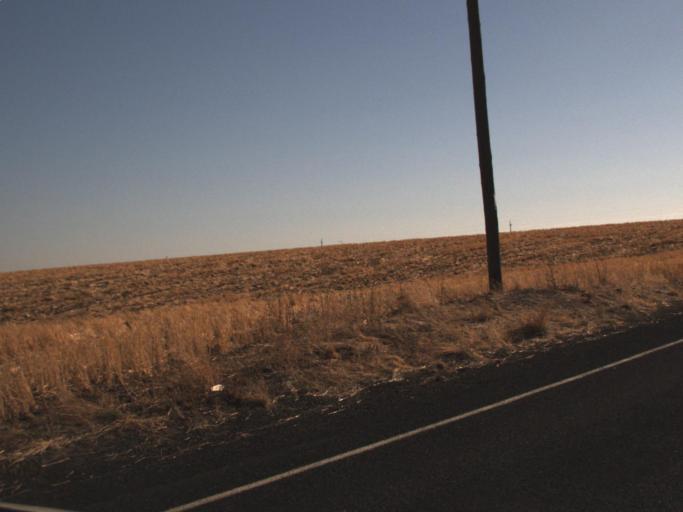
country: US
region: Washington
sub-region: Adams County
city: Ritzville
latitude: 47.0314
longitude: -118.6633
